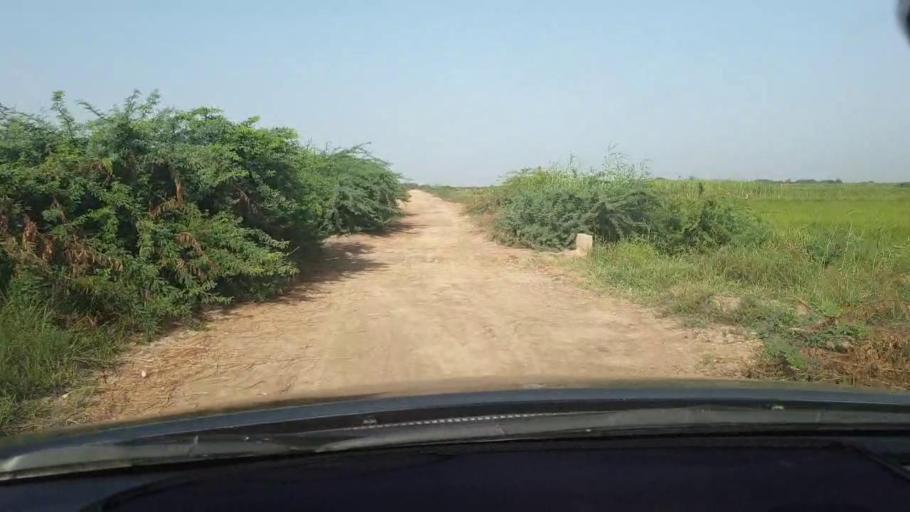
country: PK
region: Sindh
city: Tando Bago
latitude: 24.6740
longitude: 69.1883
